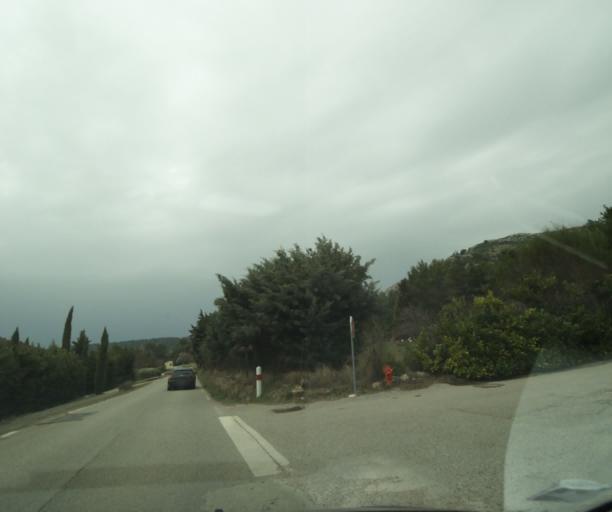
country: FR
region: Provence-Alpes-Cote d'Azur
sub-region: Departement des Bouches-du-Rhone
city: Saint-Marc-Jaumegarde
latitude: 43.5554
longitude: 5.5719
